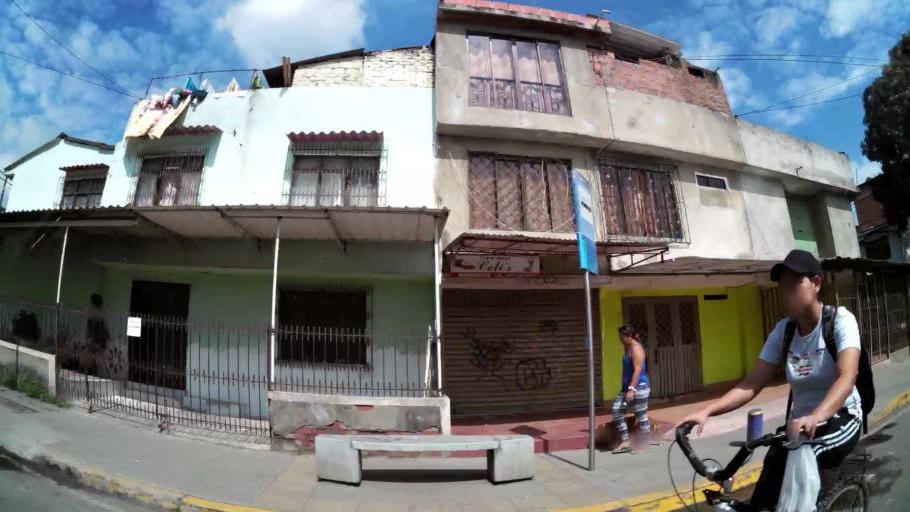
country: CO
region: Valle del Cauca
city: Cali
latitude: 3.4920
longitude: -76.4922
